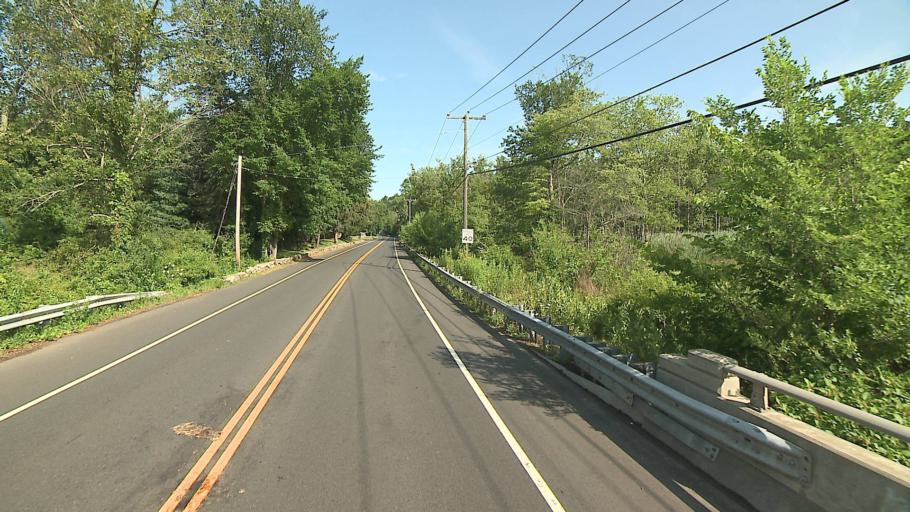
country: US
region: Connecticut
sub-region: Fairfield County
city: Ridgefield
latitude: 41.3055
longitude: -73.4631
